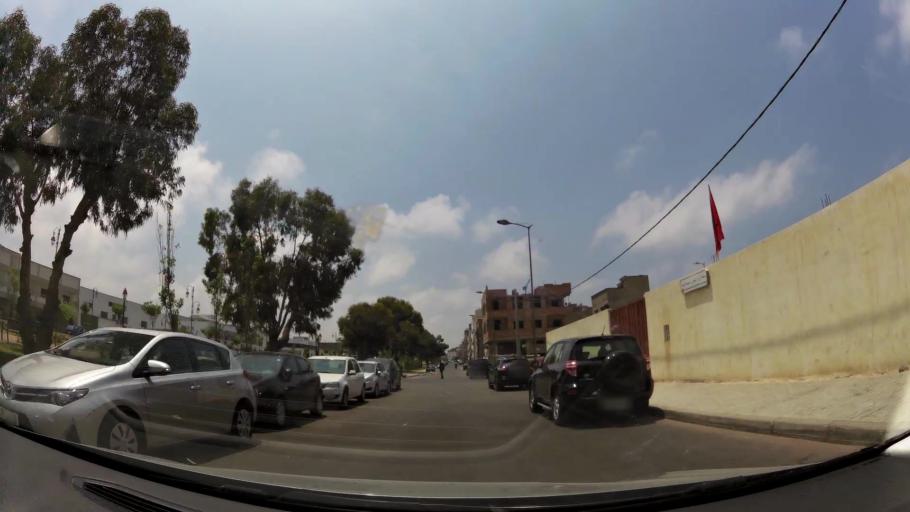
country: MA
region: Rabat-Sale-Zemmour-Zaer
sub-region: Rabat
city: Rabat
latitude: 33.9862
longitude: -6.8743
